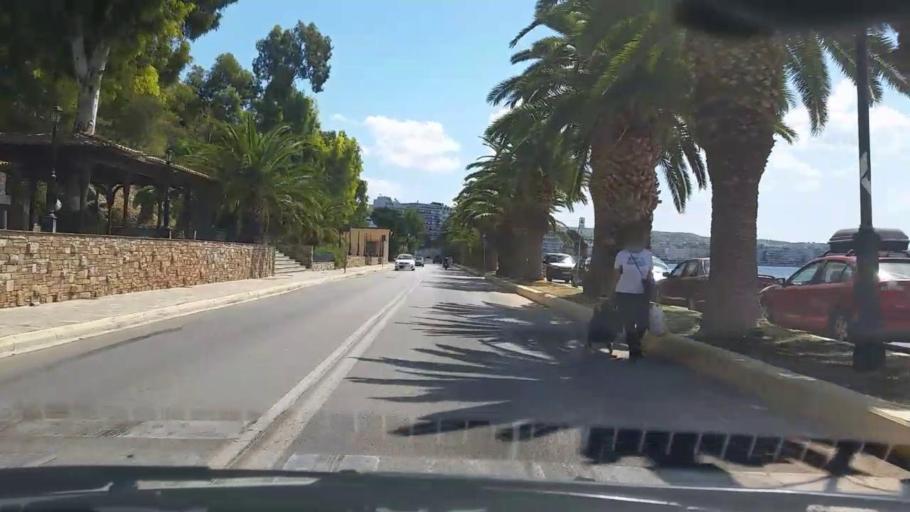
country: GR
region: Peloponnese
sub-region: Nomos Korinthias
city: Loutraki
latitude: 37.9832
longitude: 22.9688
